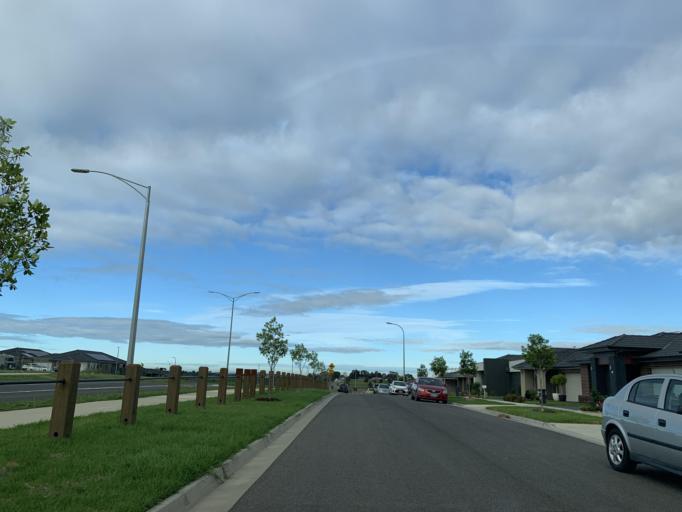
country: AU
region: Victoria
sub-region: Casey
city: Cranbourne East
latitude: -38.1244
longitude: 145.3451
